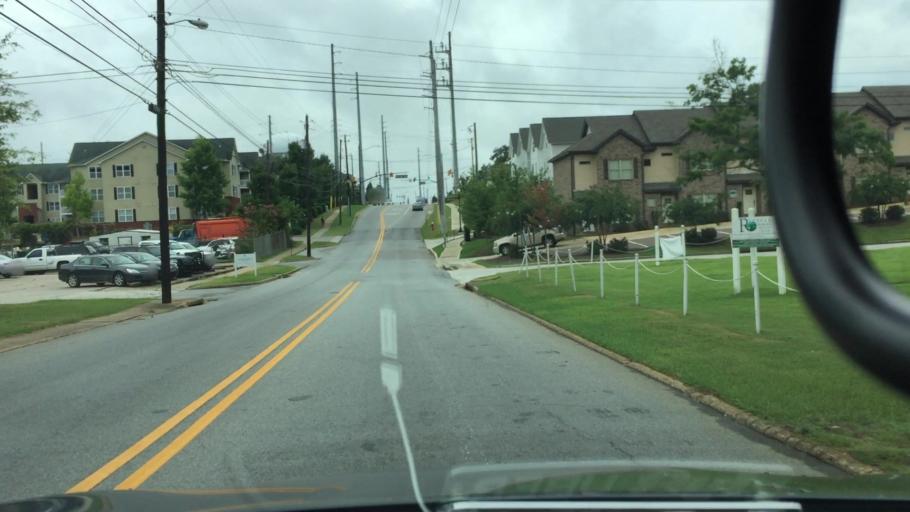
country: US
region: Alabama
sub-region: Lee County
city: Auburn
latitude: 32.6126
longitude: -85.4904
